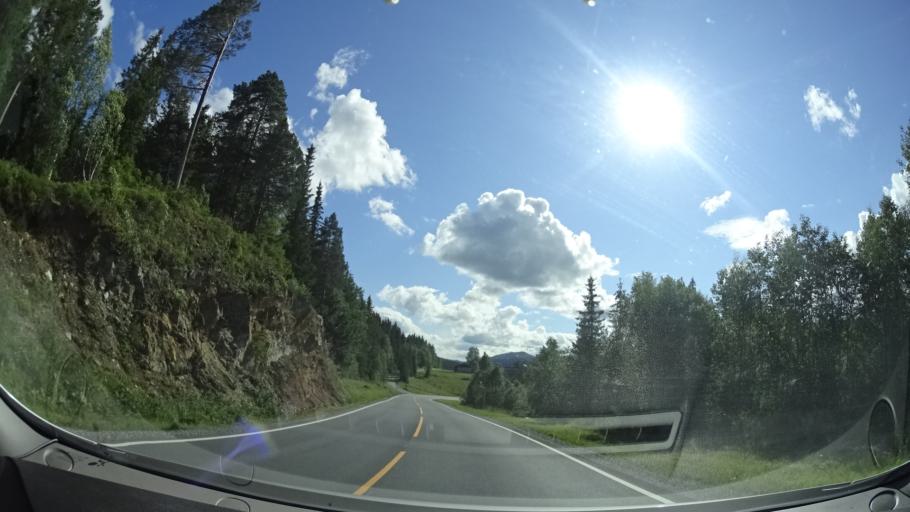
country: NO
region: Sor-Trondelag
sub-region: Snillfjord
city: Krokstadora
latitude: 63.2407
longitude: 9.6085
